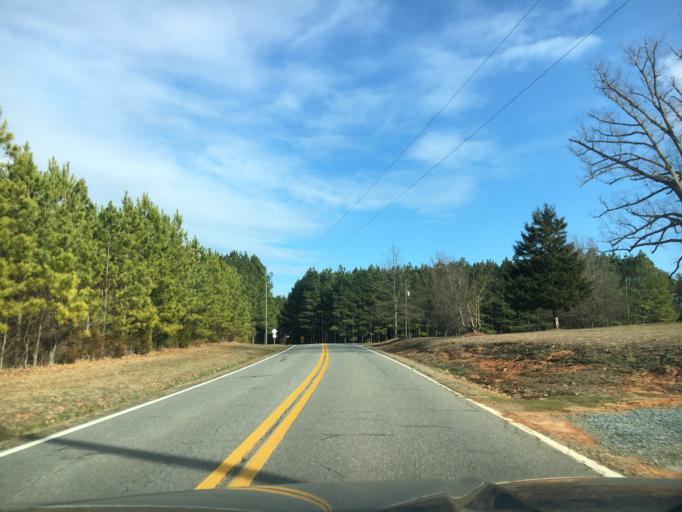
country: US
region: Virginia
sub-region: Halifax County
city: South Boston
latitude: 36.7326
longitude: -78.8677
